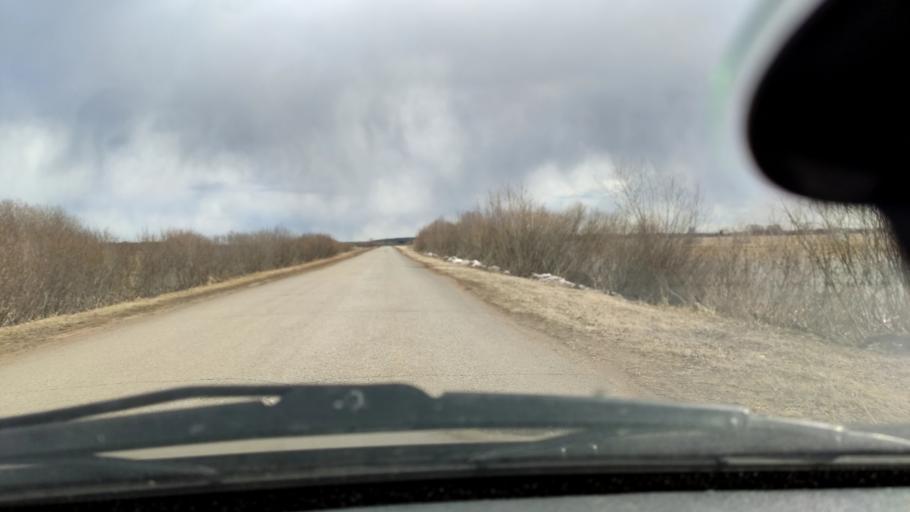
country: RU
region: Bashkortostan
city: Mikhaylovka
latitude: 54.9776
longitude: 55.7749
